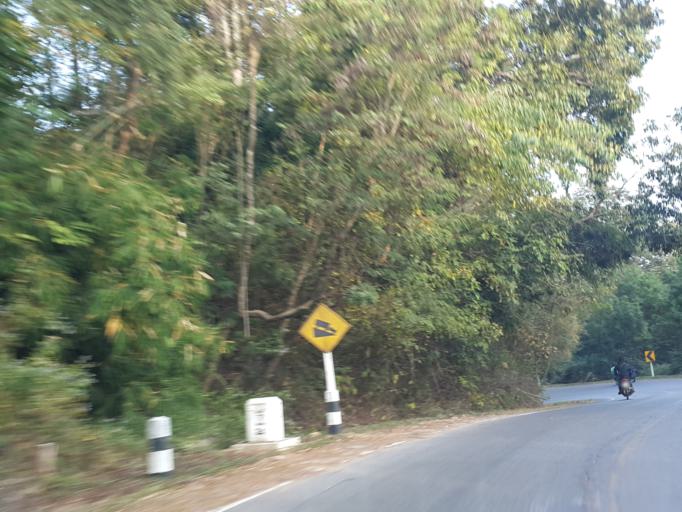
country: TH
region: Chiang Mai
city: Chiang Mai
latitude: 18.9082
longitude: 98.8924
